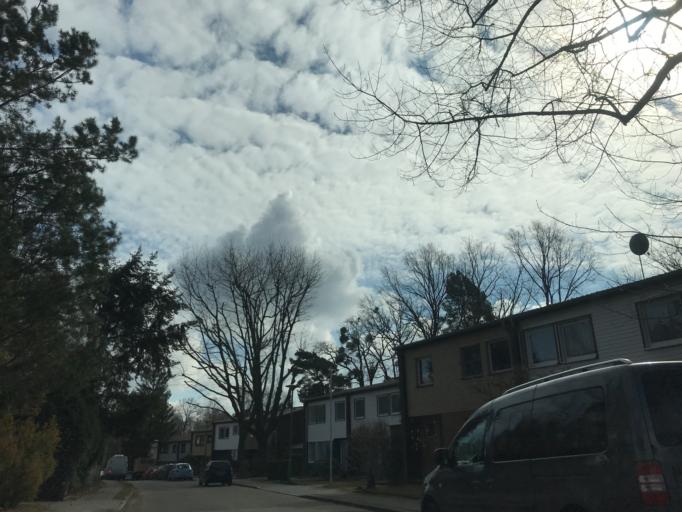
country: DE
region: Berlin
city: Kladow
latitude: 52.4552
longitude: 13.1473
